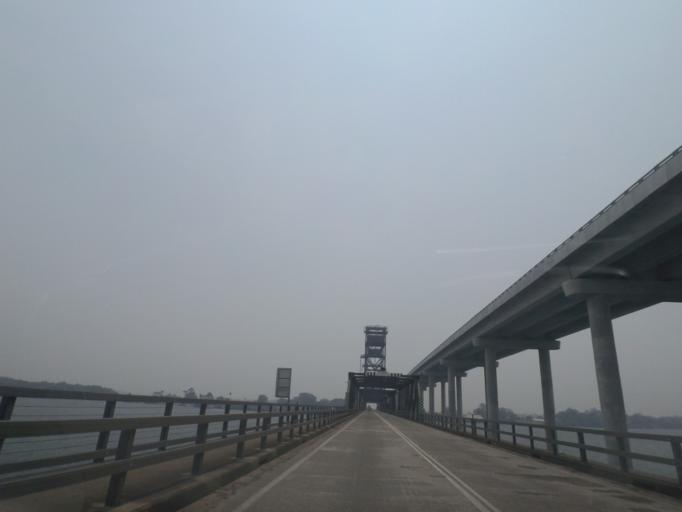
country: AU
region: New South Wales
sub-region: Clarence Valley
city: Maclean
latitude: -29.4315
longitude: 153.2408
